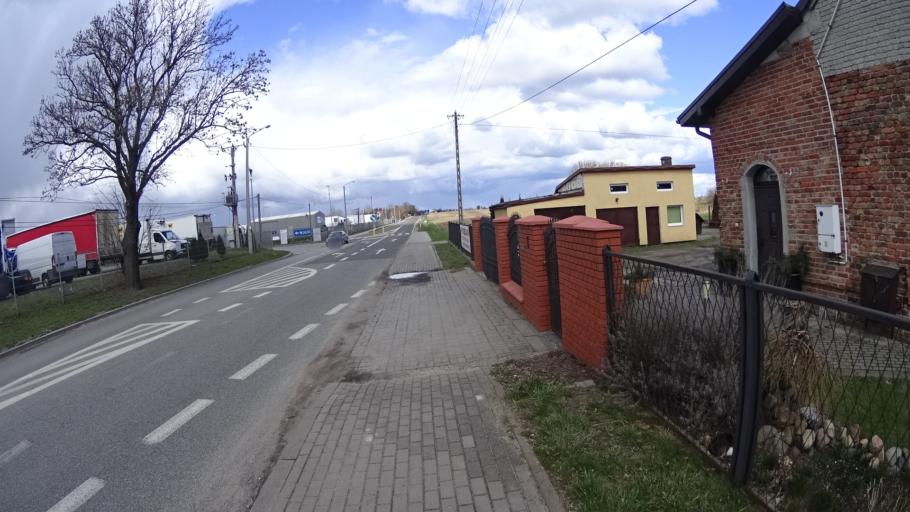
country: PL
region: Masovian Voivodeship
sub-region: Powiat warszawski zachodni
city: Jozefow
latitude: 52.2131
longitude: 20.6910
